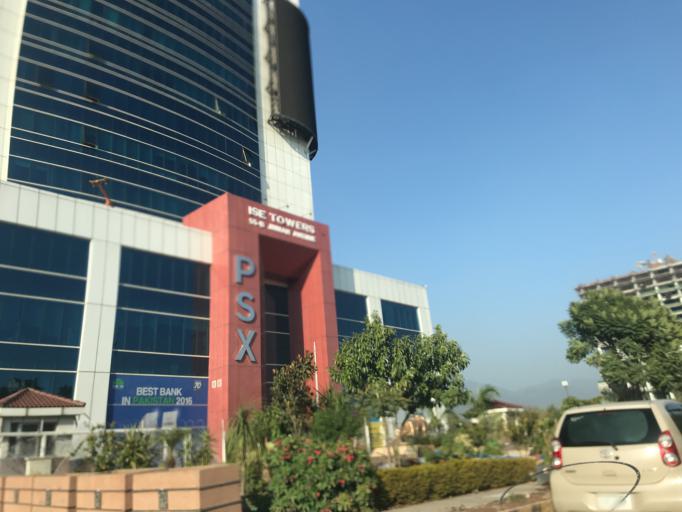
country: PK
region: Islamabad
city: Islamabad
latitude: 33.7115
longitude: 73.0579
